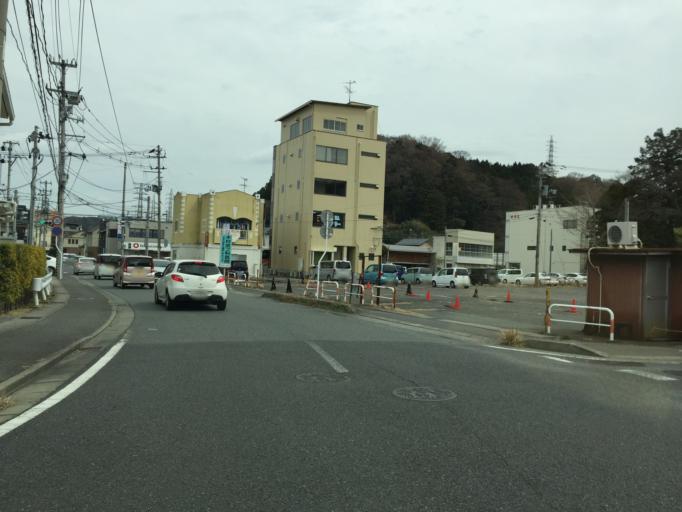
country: JP
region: Fukushima
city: Iwaki
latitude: 37.0465
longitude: 140.8923
